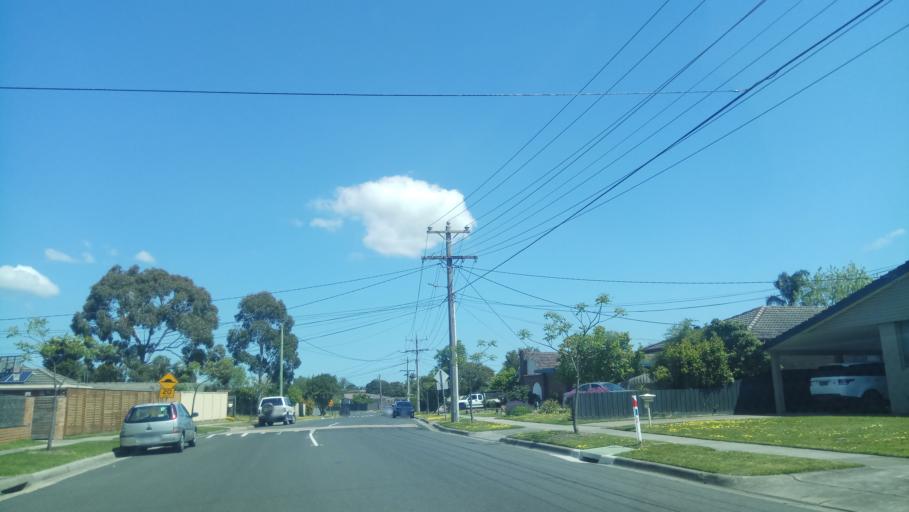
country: AU
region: Victoria
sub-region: Kingston
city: Dingley Village
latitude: -37.9848
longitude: 145.1391
